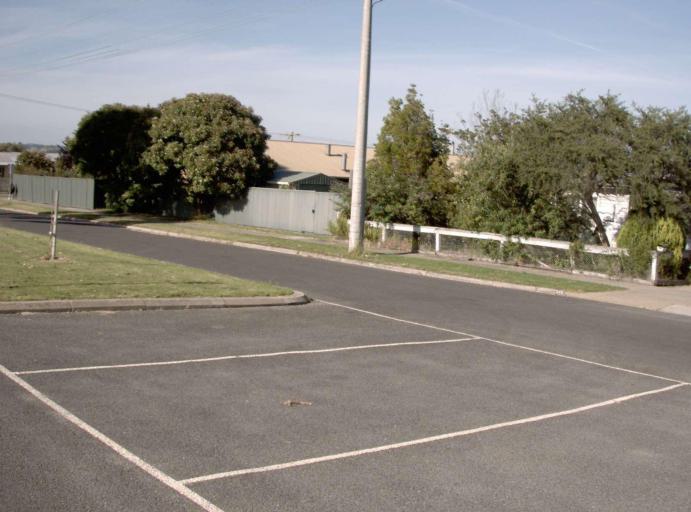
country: AU
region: Victoria
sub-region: East Gippsland
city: Lakes Entrance
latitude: -37.6968
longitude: 148.4574
